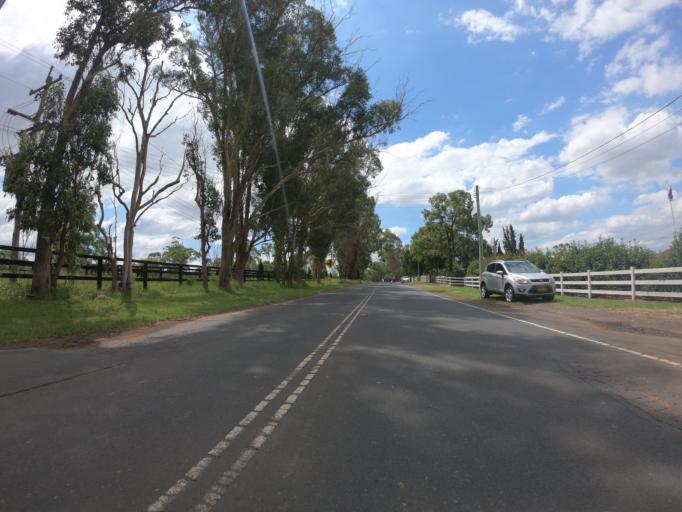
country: AU
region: New South Wales
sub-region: Penrith Municipality
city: Kingswood Park
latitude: -33.8194
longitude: 150.7605
